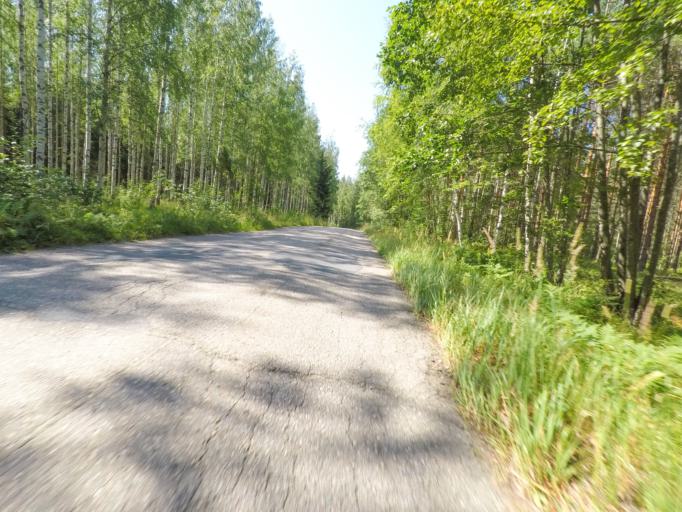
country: FI
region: Southern Savonia
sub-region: Mikkeli
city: Puumala
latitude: 61.4223
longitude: 28.1236
